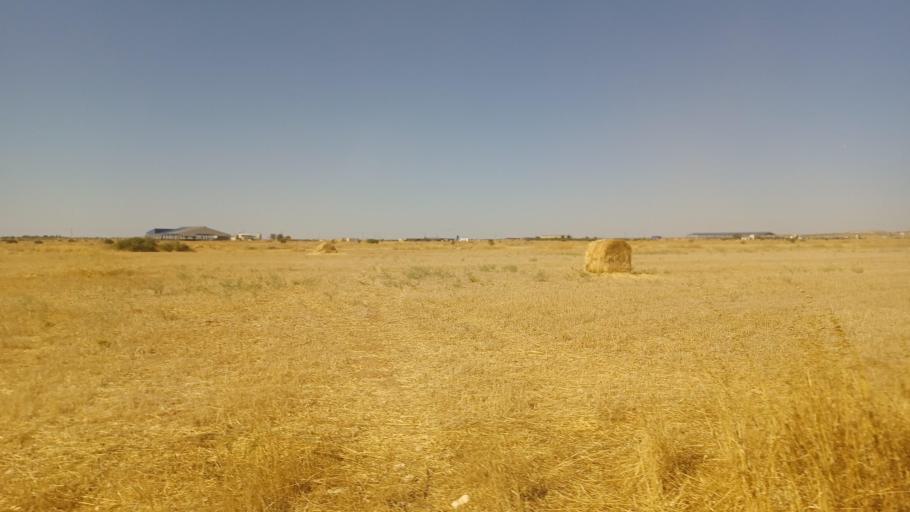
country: CY
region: Larnaka
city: Pergamos
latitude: 35.0392
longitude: 33.6917
